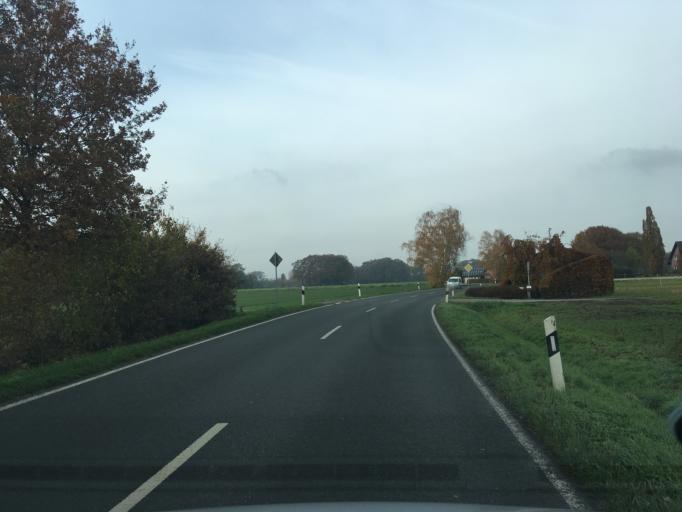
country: DE
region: North Rhine-Westphalia
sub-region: Regierungsbezirk Munster
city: Velen
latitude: 51.9060
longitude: 6.9708
